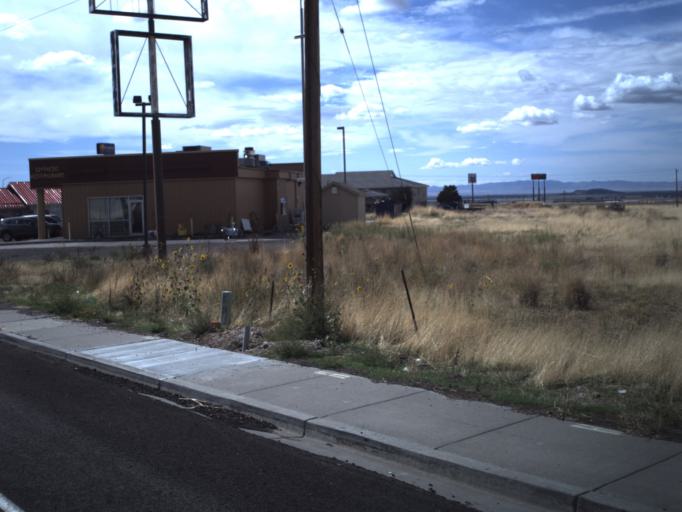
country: US
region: Utah
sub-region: Millard County
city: Fillmore
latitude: 38.9500
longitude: -112.3446
